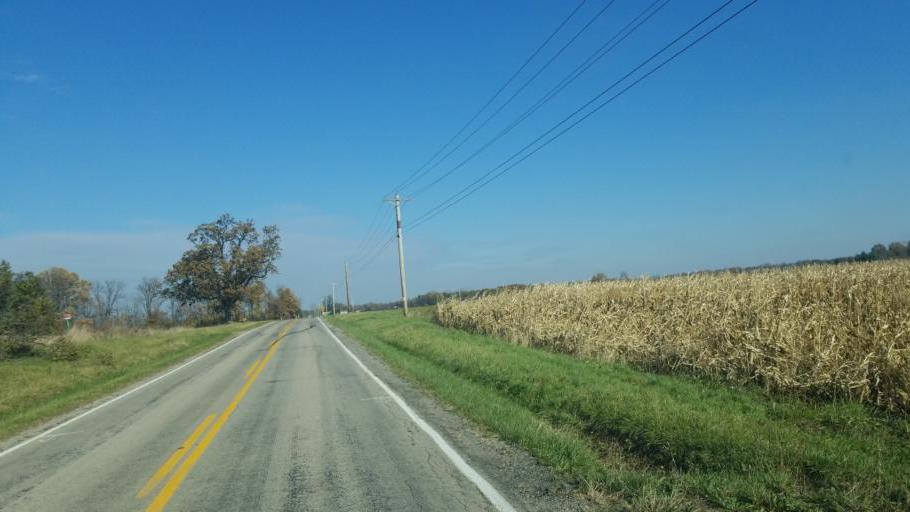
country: US
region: Ohio
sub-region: Lorain County
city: Camden
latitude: 41.2073
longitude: -82.2637
